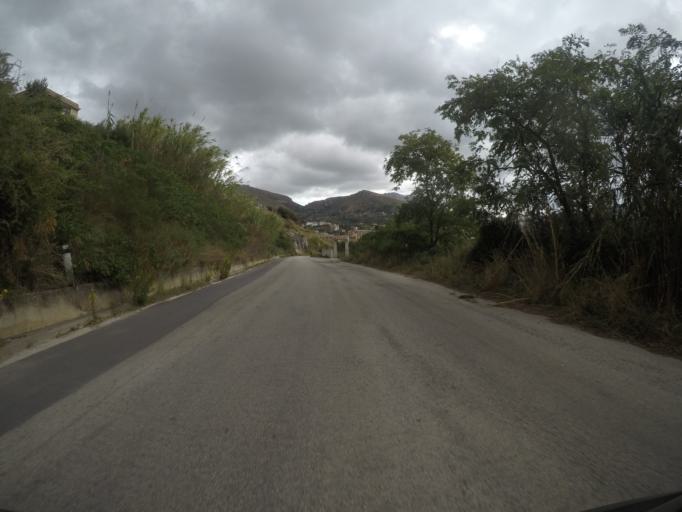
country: IT
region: Sicily
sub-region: Palermo
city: Montelepre
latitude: 38.0939
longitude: 13.1729
